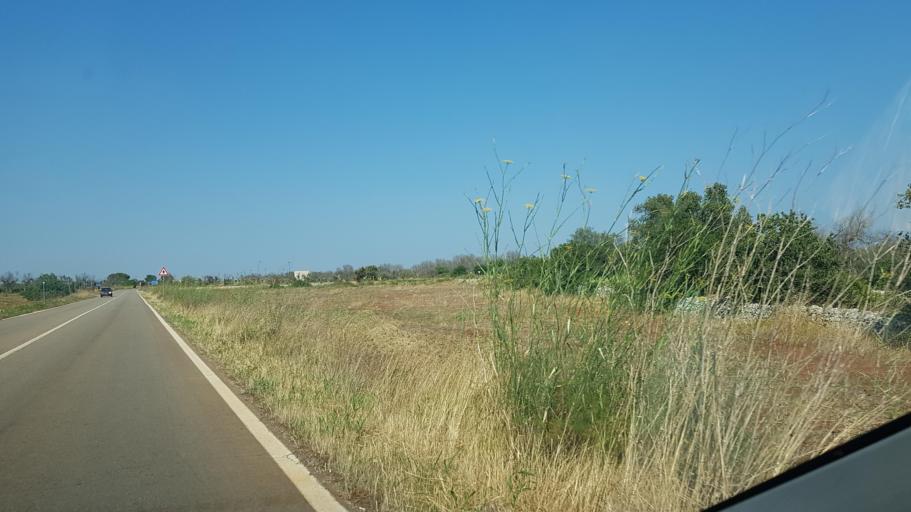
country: IT
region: Apulia
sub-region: Provincia di Lecce
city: Acquarica del Capo
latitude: 39.8850
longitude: 18.2372
